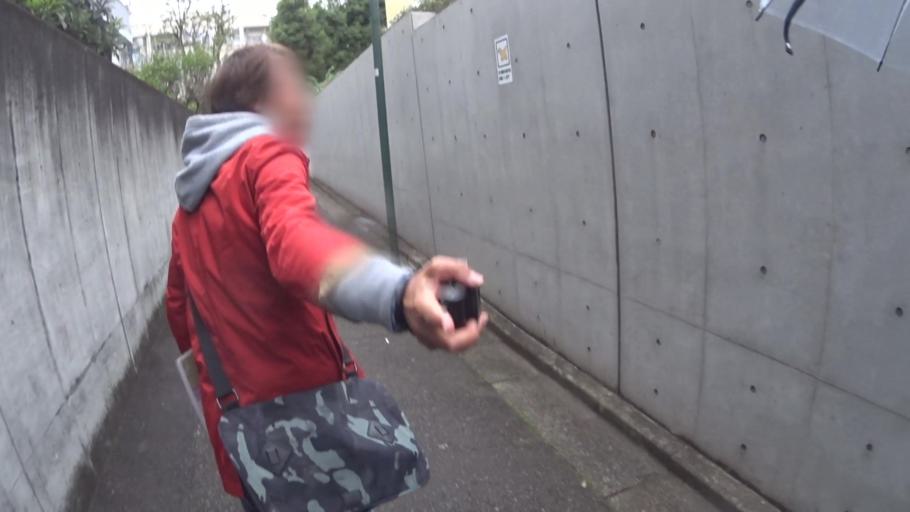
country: JP
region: Tokyo
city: Tokyo
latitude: 35.6480
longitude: 139.7310
